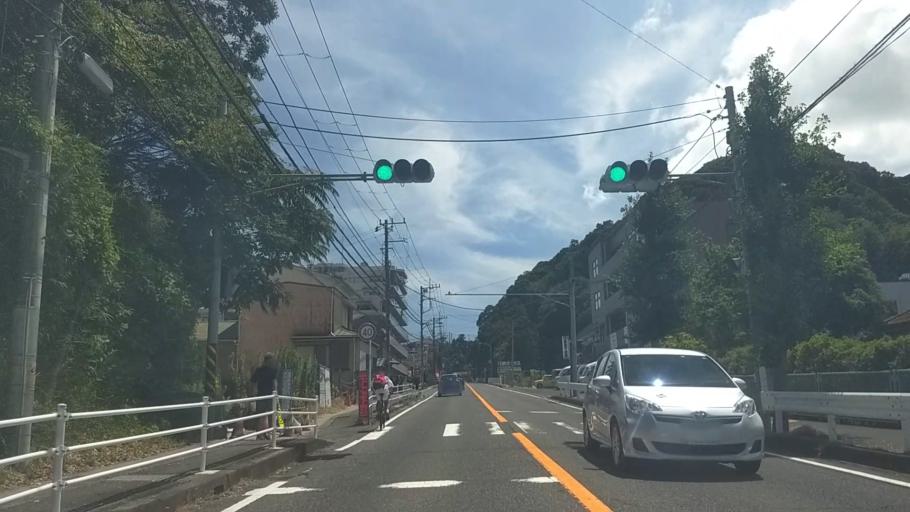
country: JP
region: Kanagawa
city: Yokosuka
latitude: 35.2499
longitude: 139.6651
